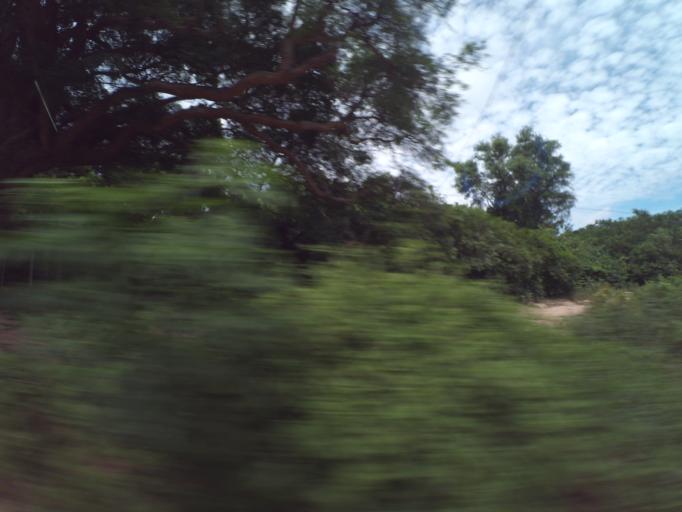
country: BO
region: Santa Cruz
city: Santa Cruz de la Sierra
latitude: -17.9224
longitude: -63.1607
